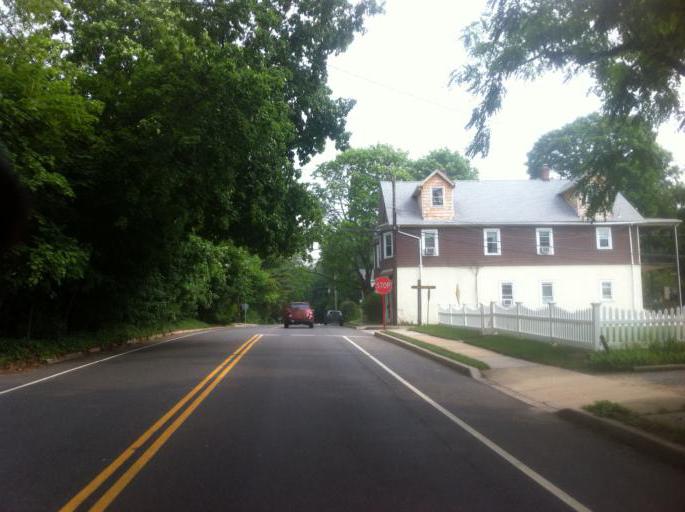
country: US
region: New York
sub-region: Nassau County
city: Locust Valley
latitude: 40.8783
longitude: -73.5788
